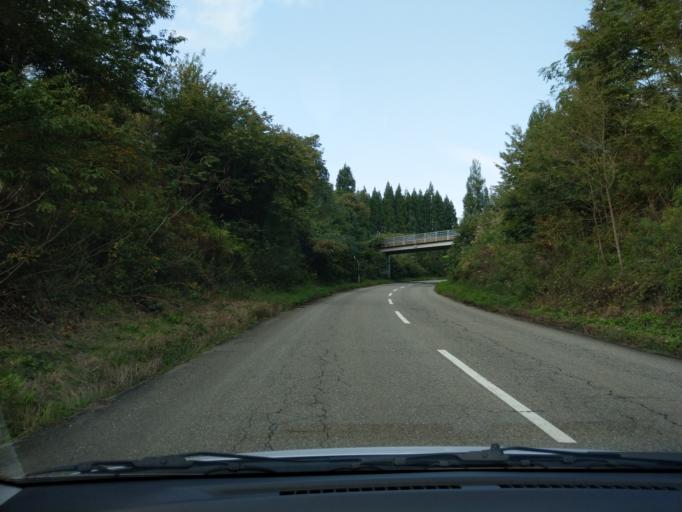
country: JP
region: Akita
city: Omagari
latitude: 39.5204
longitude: 140.2972
